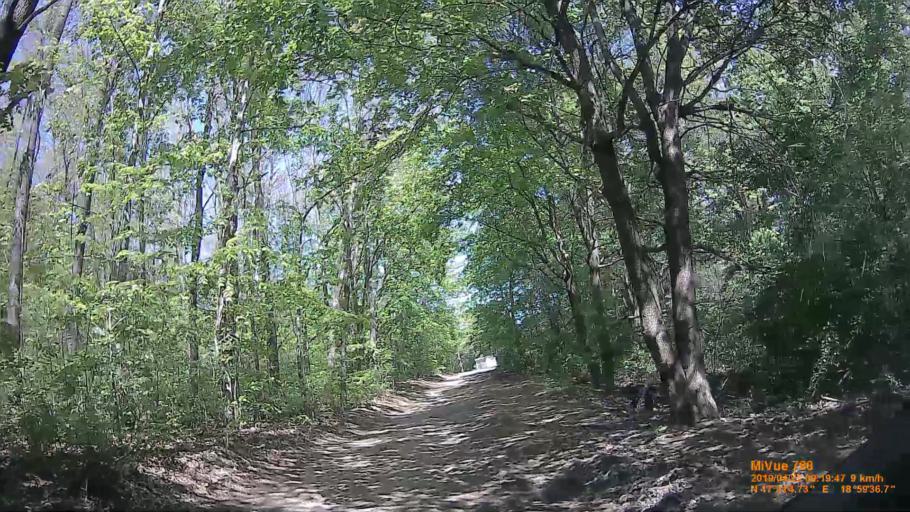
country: HU
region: Pest
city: Urom
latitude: 47.5680
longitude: 18.9935
